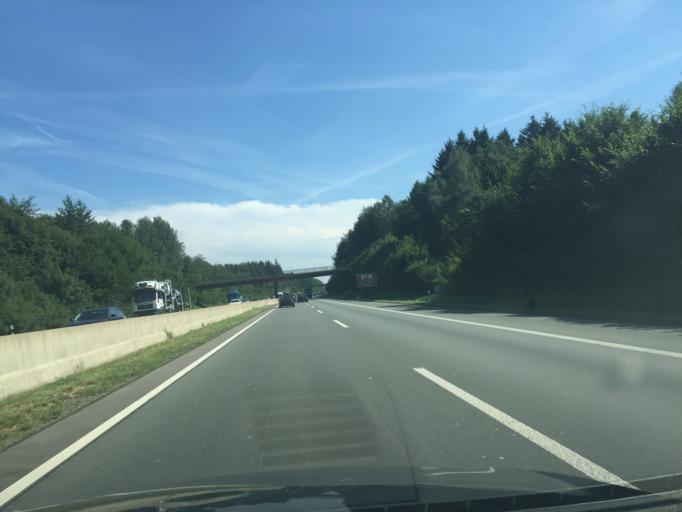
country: DE
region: North Rhine-Westphalia
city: Freudenberg
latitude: 50.9306
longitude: 7.8876
